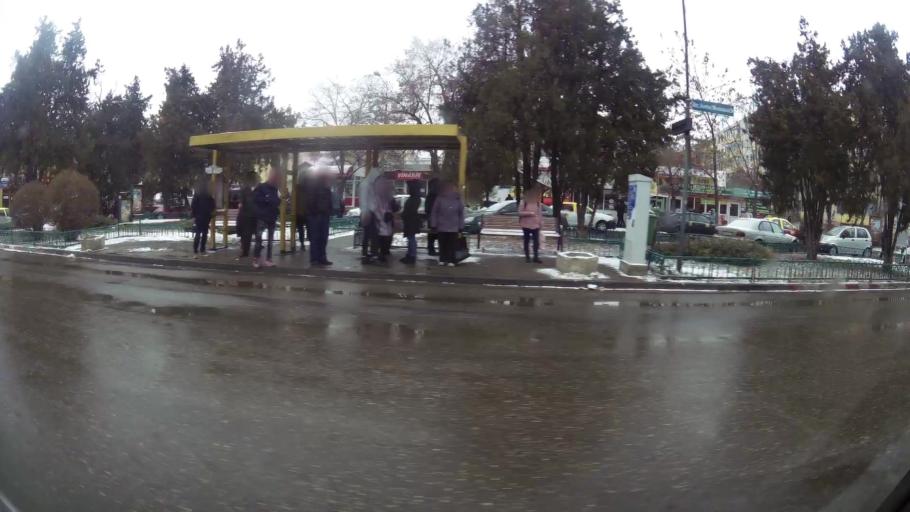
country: RO
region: Prahova
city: Ploiesti
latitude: 44.9518
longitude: 26.0109
